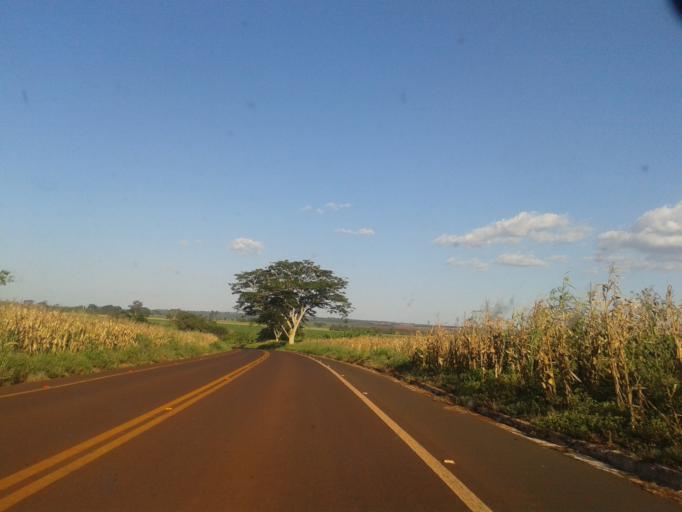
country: BR
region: Minas Gerais
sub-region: Santa Vitoria
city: Santa Vitoria
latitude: -18.7042
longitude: -49.8674
